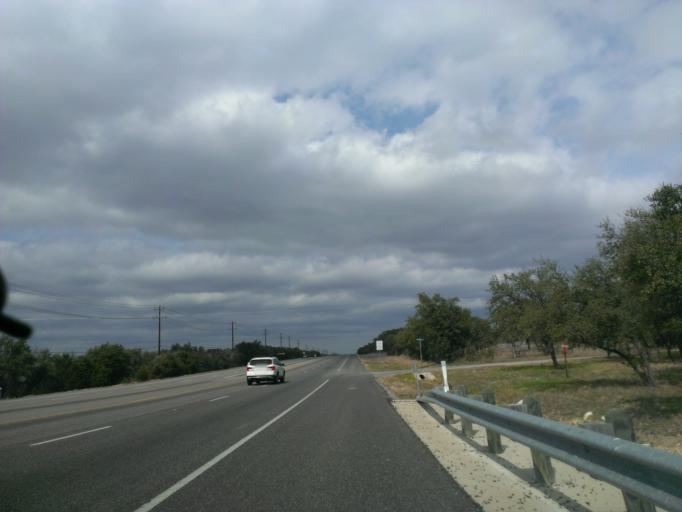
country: US
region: Texas
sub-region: Travis County
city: Briarcliff
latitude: 30.3780
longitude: -98.0813
